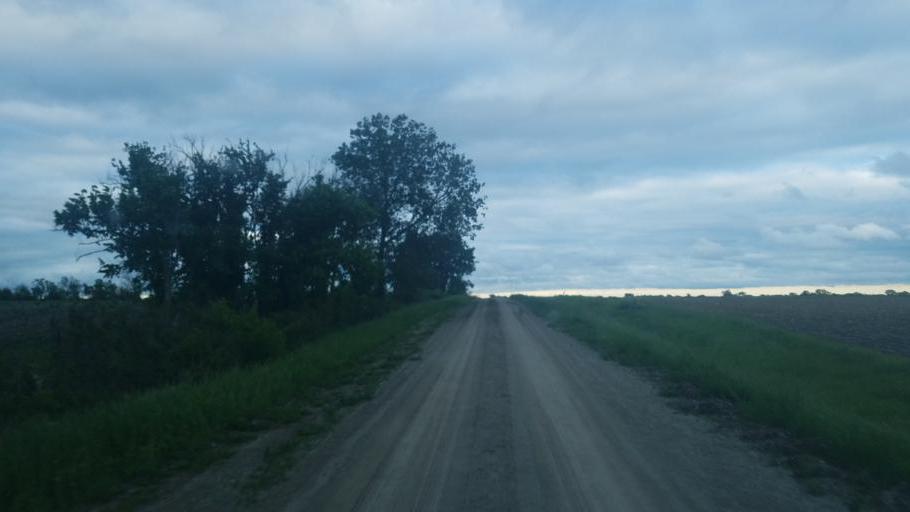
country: US
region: Iowa
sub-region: Decatur County
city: Lamoni
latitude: 40.5948
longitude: -93.9664
